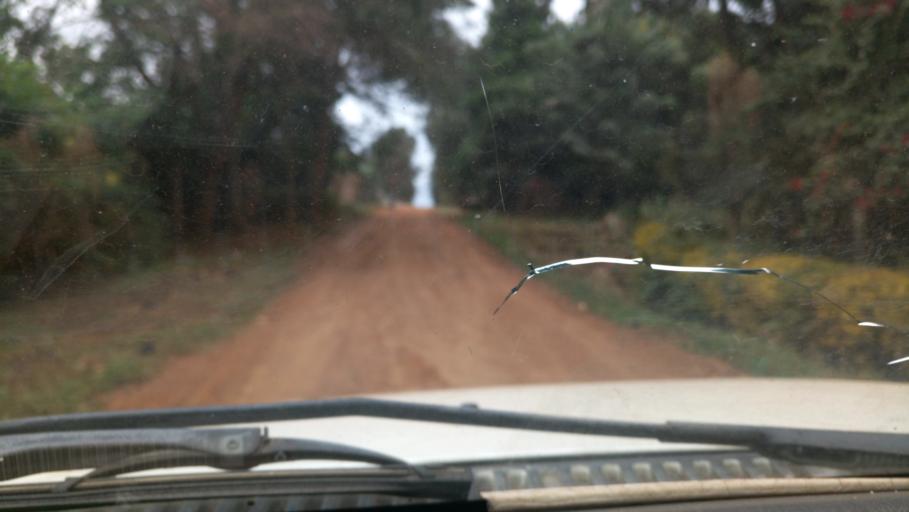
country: KE
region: Nairobi Area
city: Pumwani
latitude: -1.2278
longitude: 36.8712
